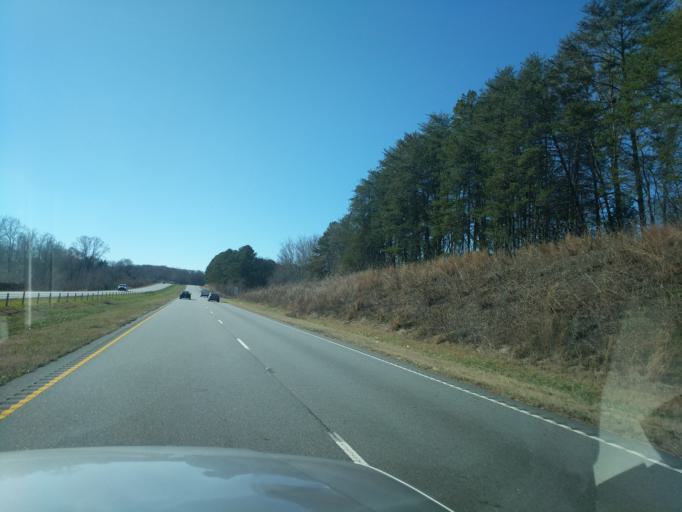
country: US
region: South Carolina
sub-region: Pickens County
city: Easley
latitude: 34.8145
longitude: -82.6120
